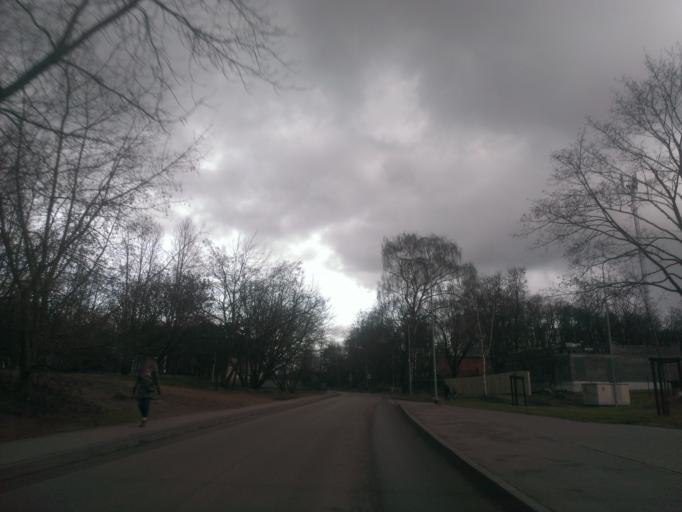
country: LV
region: Riga
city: Bolderaja
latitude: 57.0365
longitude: 24.0971
